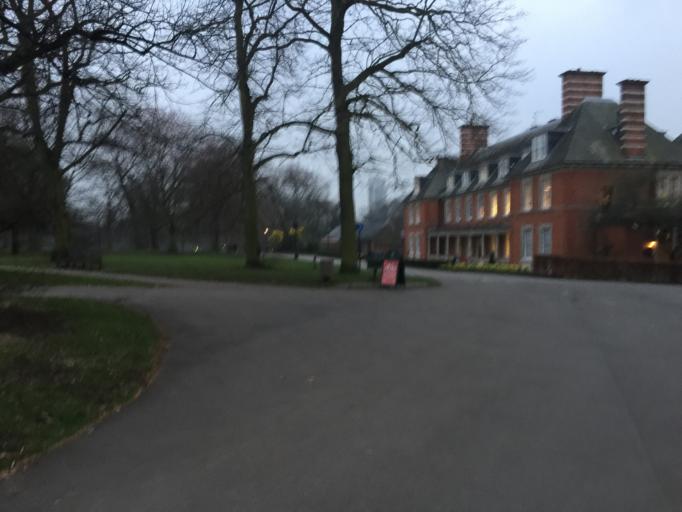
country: GB
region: England
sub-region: Greater London
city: Bayswater
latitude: 51.5087
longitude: -0.1651
